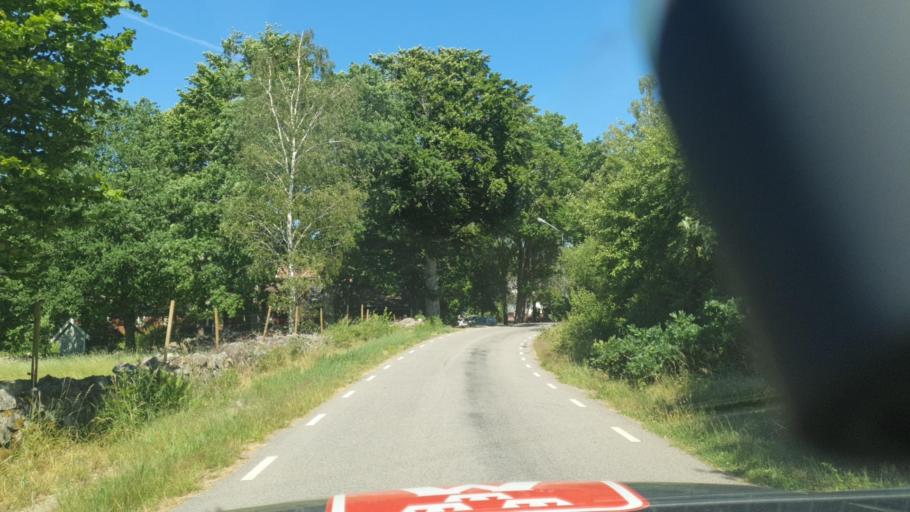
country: SE
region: Kalmar
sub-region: Torsas Kommun
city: Torsas
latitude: 56.2976
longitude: 15.9945
